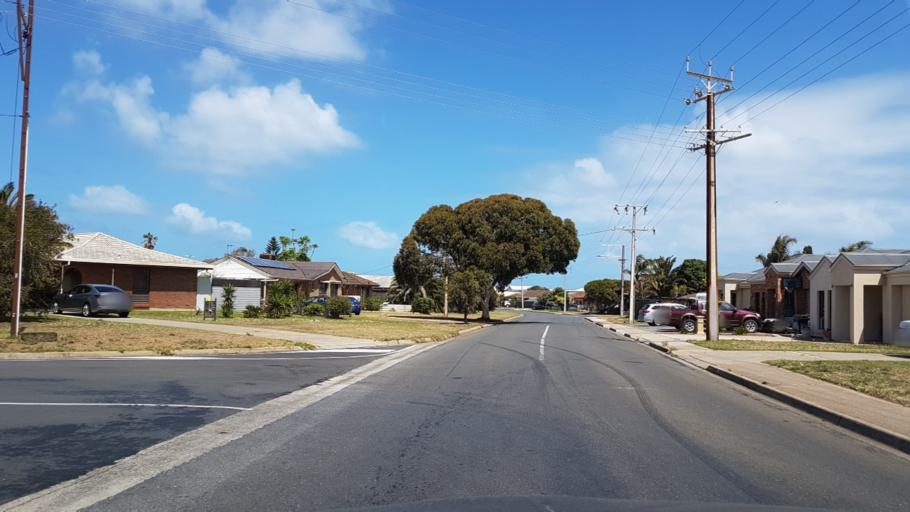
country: AU
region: South Australia
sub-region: Onkaparinga
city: Seaford
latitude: -35.1873
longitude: 138.4728
